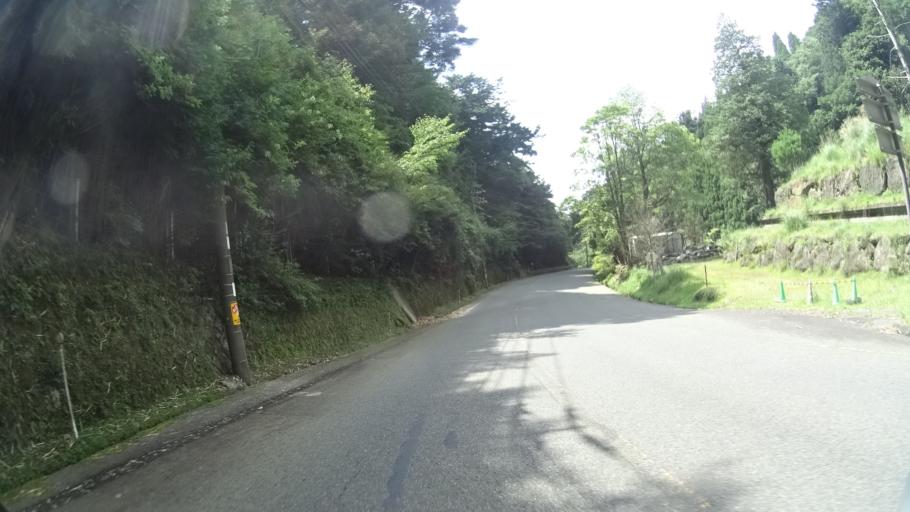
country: JP
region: Miyazaki
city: Kobayashi
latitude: 31.9015
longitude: 130.8446
